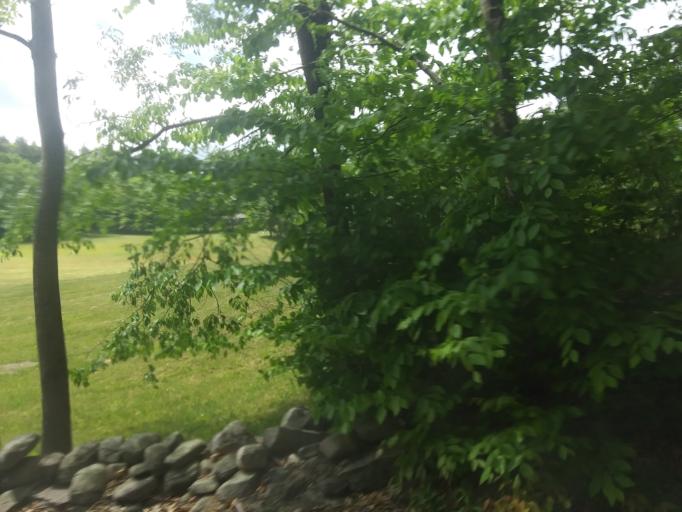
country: US
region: Massachusetts
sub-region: Franklin County
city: Shelburne Falls
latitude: 42.5932
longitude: -72.7634
